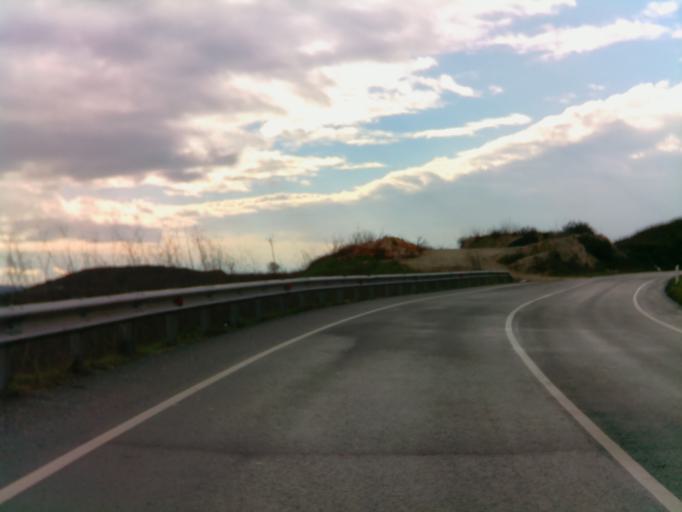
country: CY
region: Pafos
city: Pegeia
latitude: 34.9053
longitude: 32.4424
